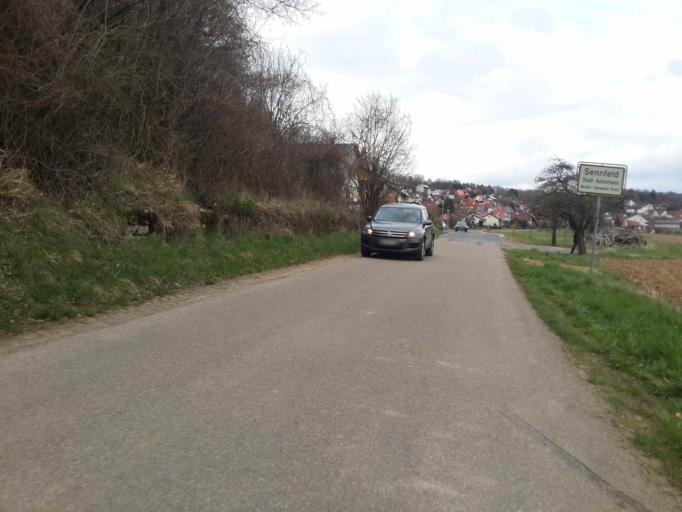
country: DE
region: Baden-Wuerttemberg
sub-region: Karlsruhe Region
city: Adelsheim
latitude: 49.3789
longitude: 9.3712
